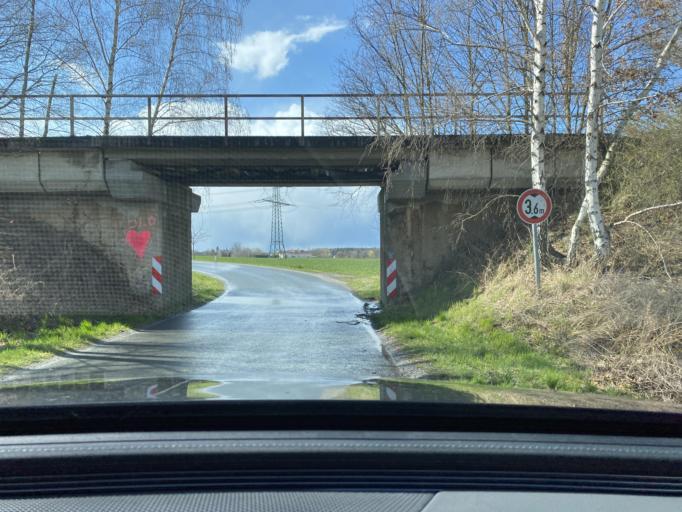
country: DE
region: Saxony
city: Radibor
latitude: 51.2479
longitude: 14.3791
